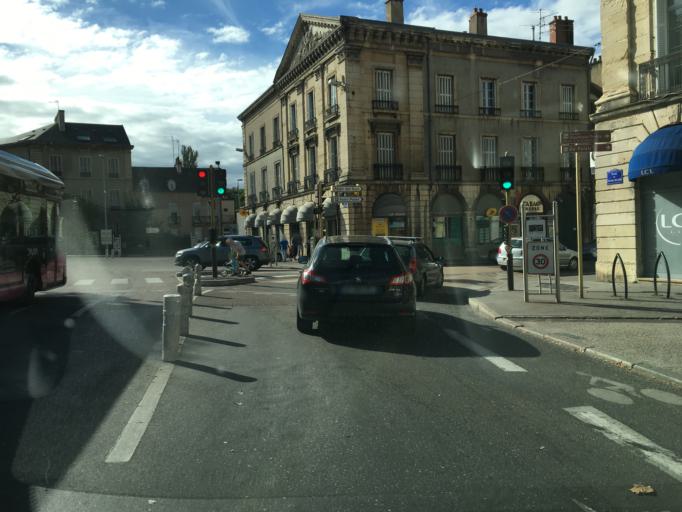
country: FR
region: Bourgogne
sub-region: Departement de la Cote-d'Or
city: Dijon
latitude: 47.3167
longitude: 5.0437
